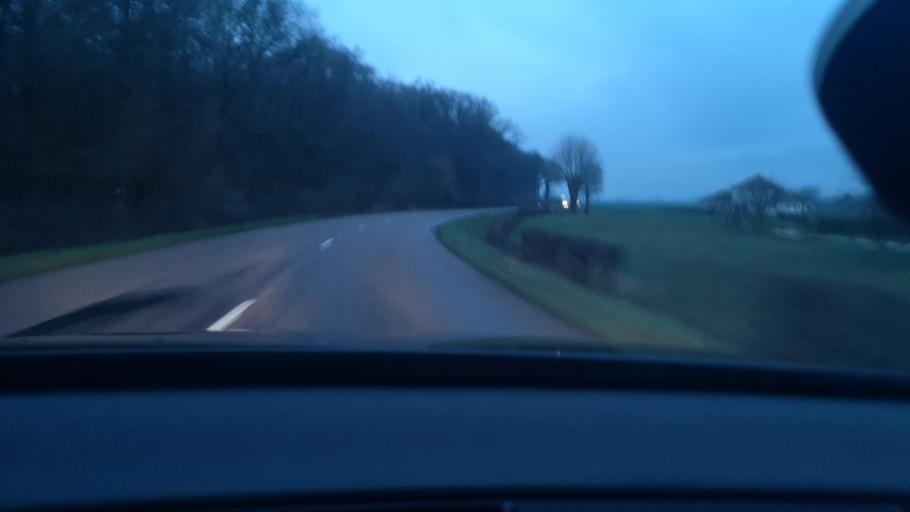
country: FR
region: Bourgogne
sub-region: Departement de Saone-et-Loire
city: Demigny
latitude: 46.9436
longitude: 4.8771
